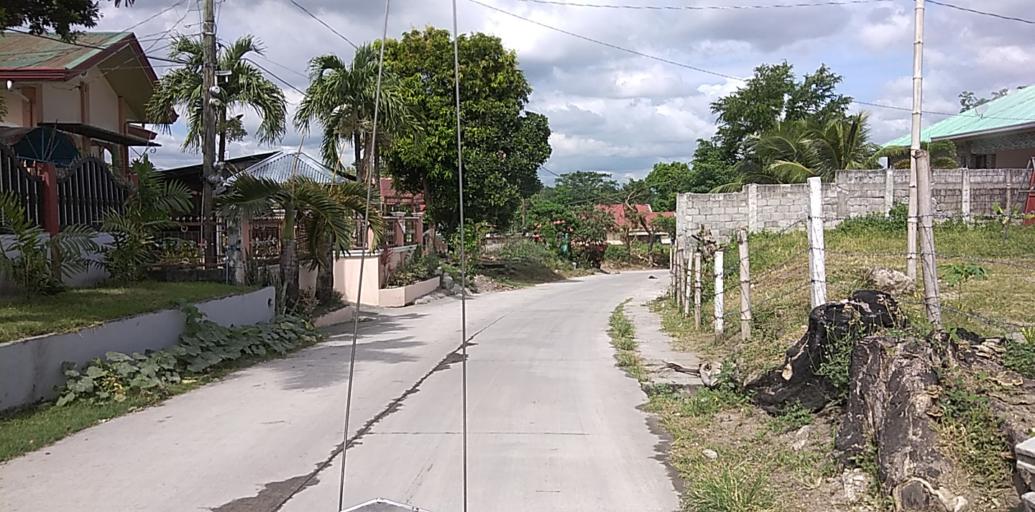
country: PH
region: Central Luzon
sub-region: Province of Pampanga
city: Porac
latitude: 15.0622
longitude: 120.5363
